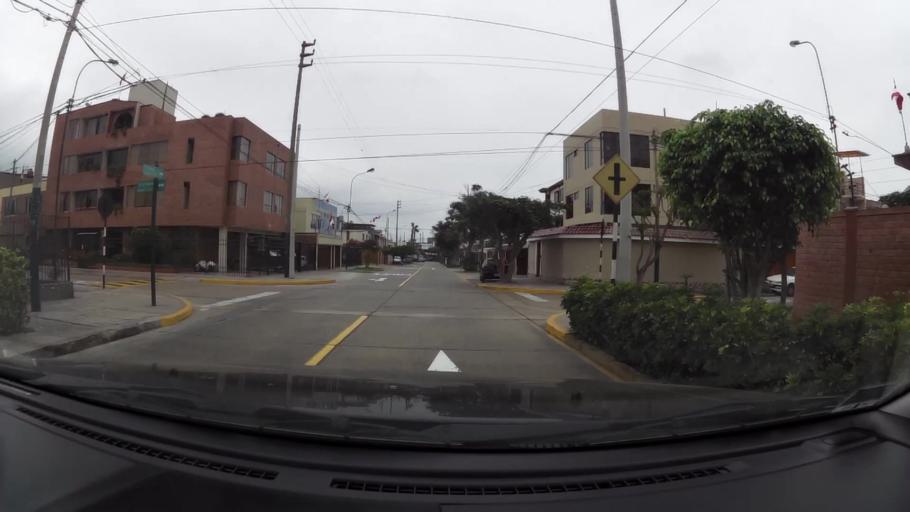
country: PE
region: Lima
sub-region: Lima
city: Surco
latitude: -12.1266
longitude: -76.9976
